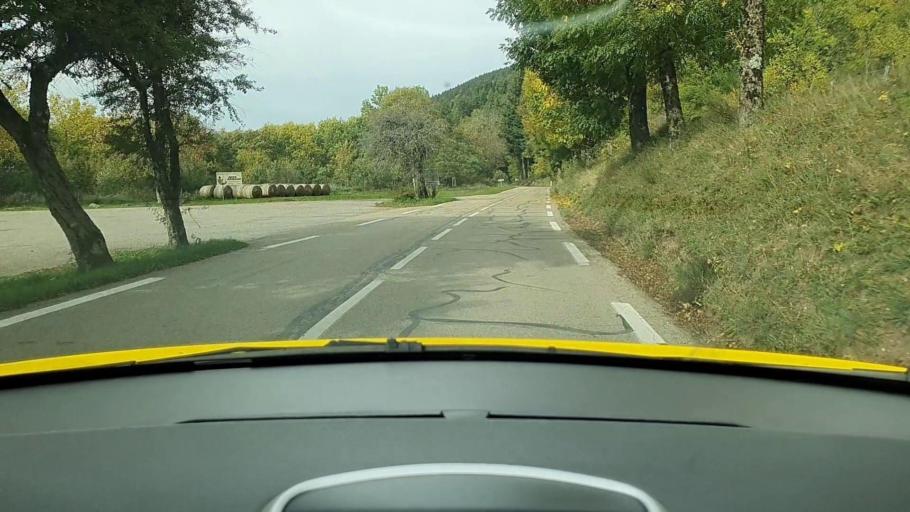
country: FR
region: Languedoc-Roussillon
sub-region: Departement de la Lozere
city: Meyrueis
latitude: 44.1226
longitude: 3.4800
